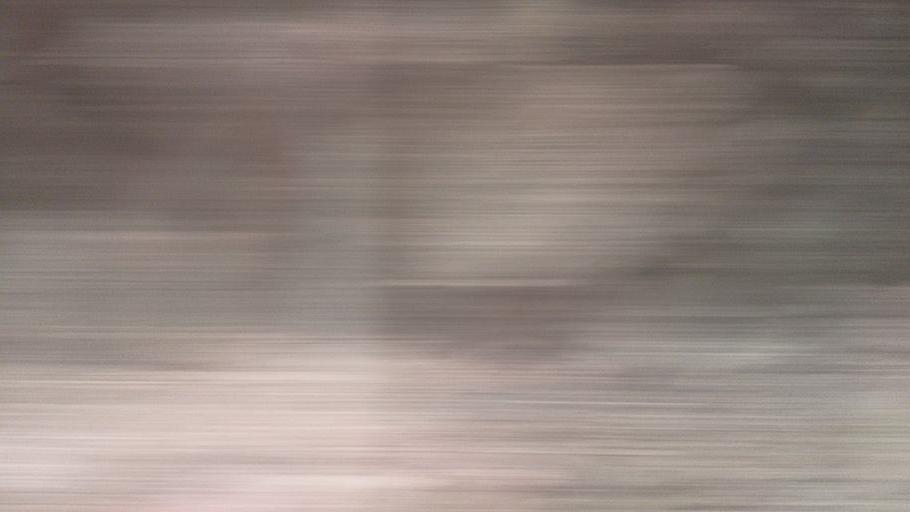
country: PT
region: Guarda
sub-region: Fornos de Algodres
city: Fornos de Algodres
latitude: 40.5971
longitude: -7.5578
